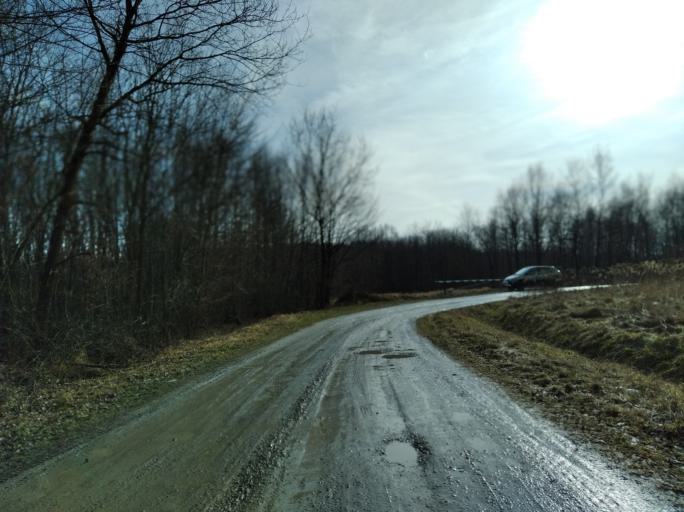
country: PL
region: Subcarpathian Voivodeship
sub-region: Powiat brzozowski
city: Gorki
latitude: 49.6401
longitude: 22.0615
